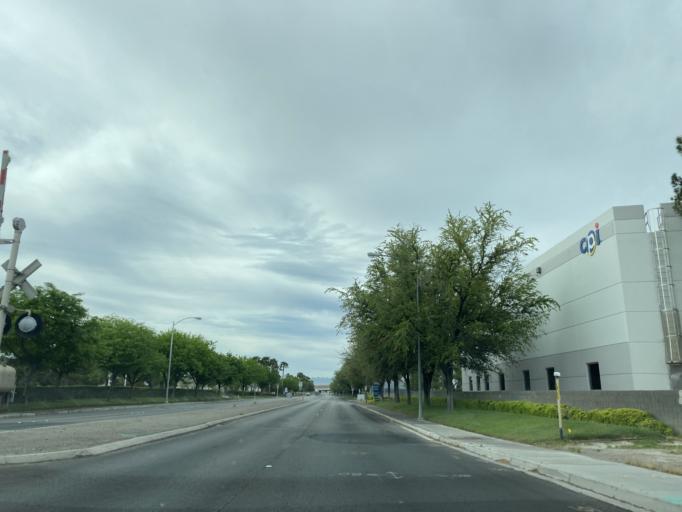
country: US
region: Nevada
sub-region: Clark County
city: Paradise
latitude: 36.0673
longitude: -115.1413
